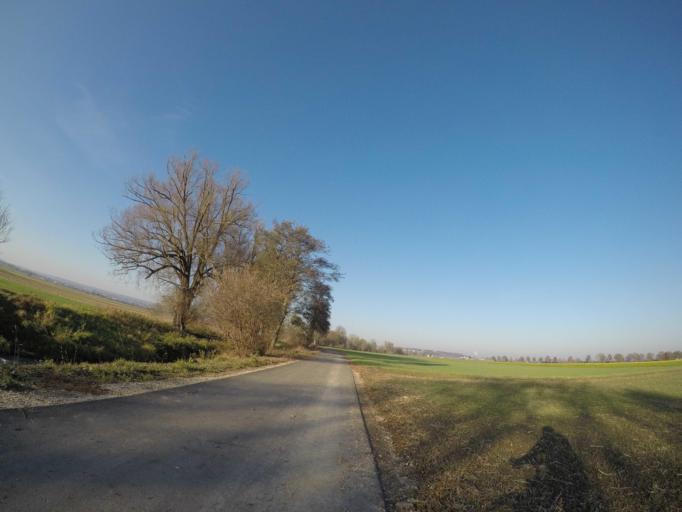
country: DE
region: Baden-Wuerttemberg
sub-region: Tuebingen Region
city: Unterstadion
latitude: 48.2103
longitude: 9.6816
